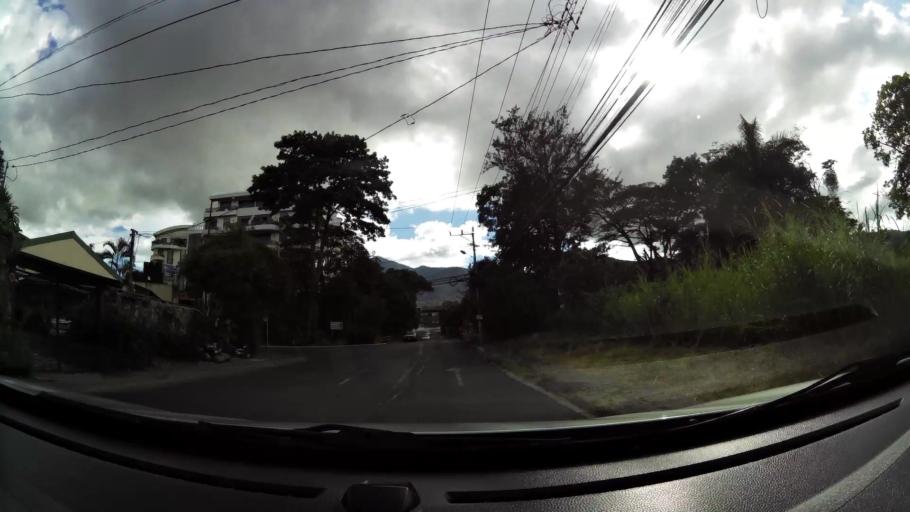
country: CR
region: San Jose
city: San Rafael
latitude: 9.9235
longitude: -84.1361
